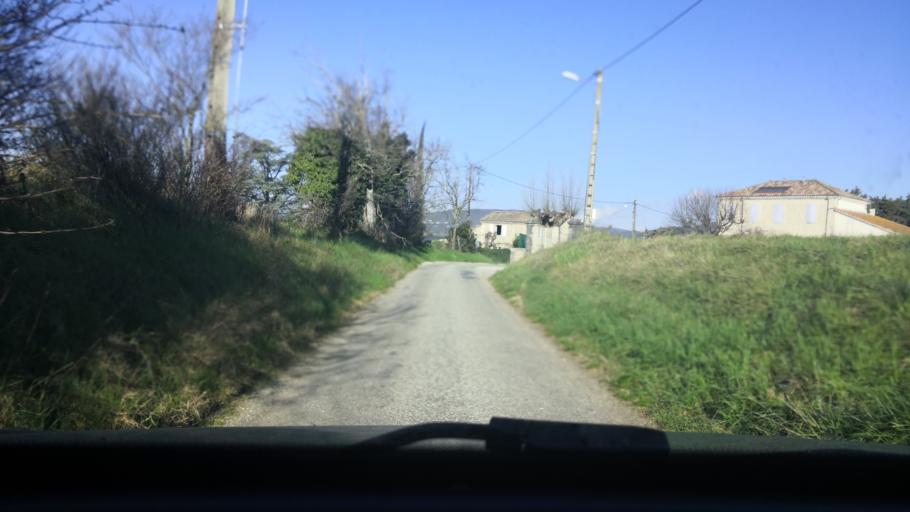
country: FR
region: Rhone-Alpes
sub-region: Departement de la Drome
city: Sauzet
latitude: 44.5792
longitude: 4.8270
